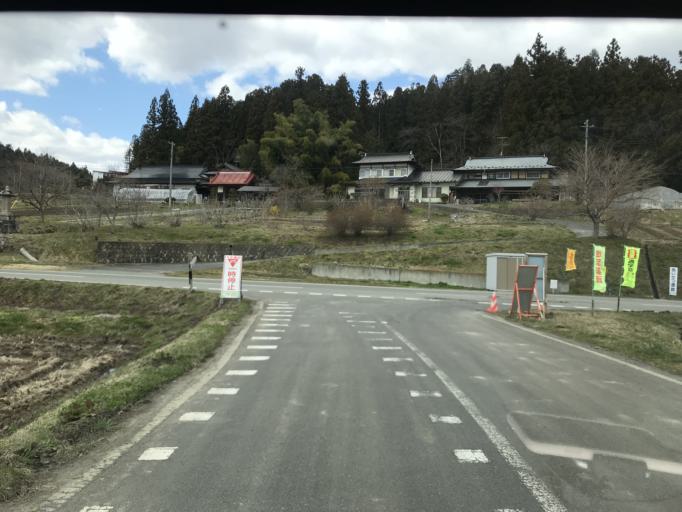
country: JP
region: Iwate
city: Ichinoseki
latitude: 38.9603
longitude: 141.0881
